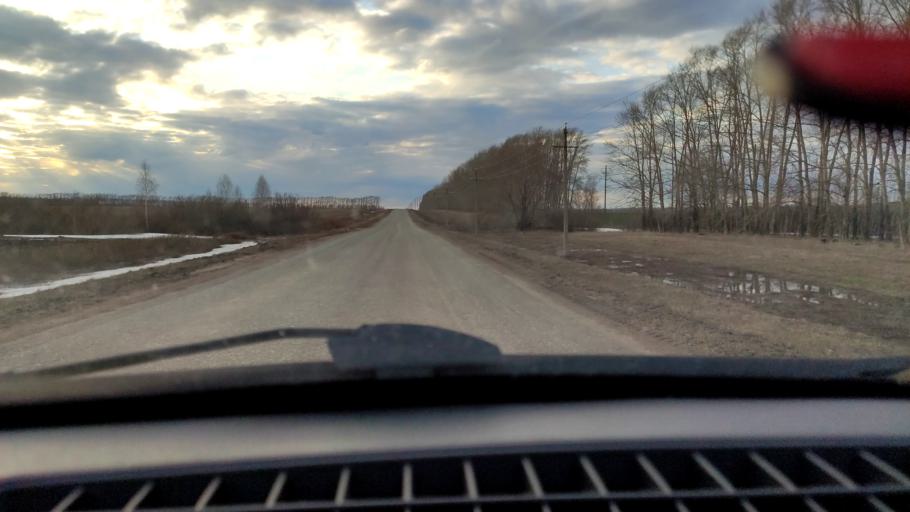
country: RU
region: Bashkortostan
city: Tolbazy
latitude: 53.9881
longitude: 55.7919
